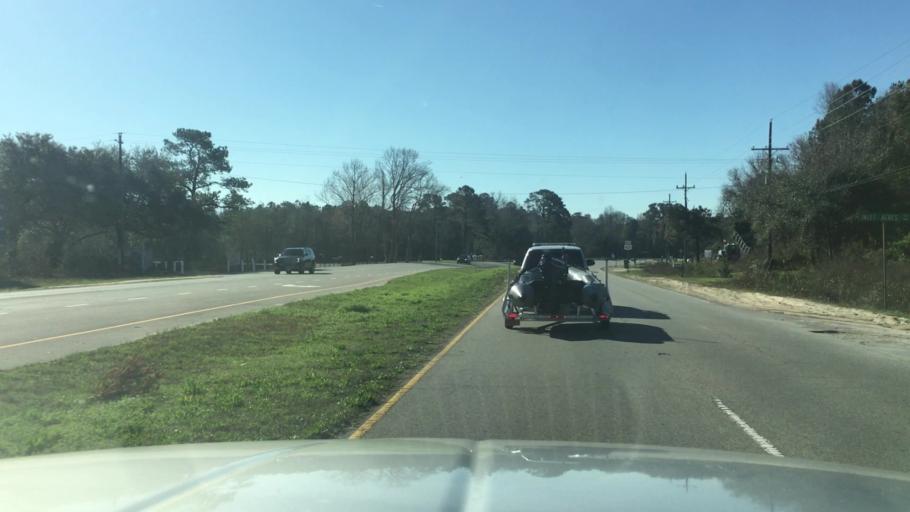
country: US
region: North Carolina
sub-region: New Hanover County
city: Sea Breeze
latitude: 34.0796
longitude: -77.8946
